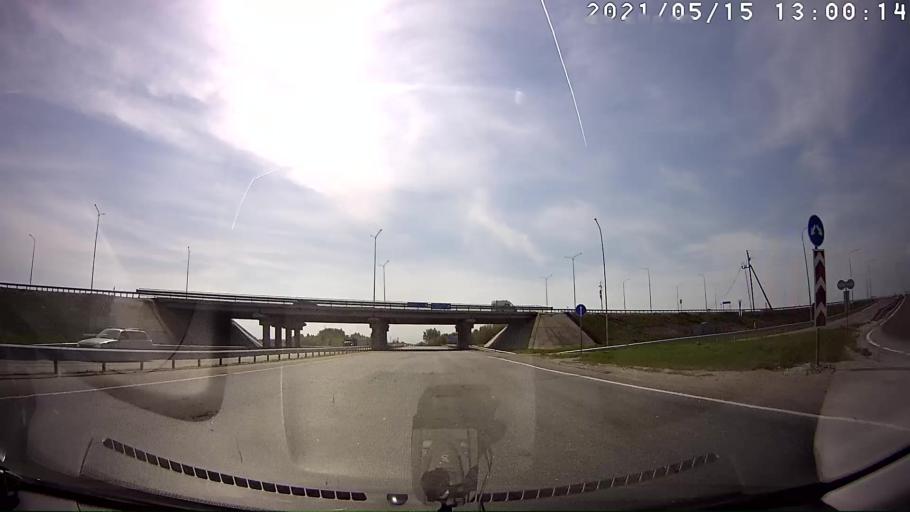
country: RU
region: Mariy-El
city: Yoshkar-Ola
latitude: 56.6802
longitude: 48.0243
